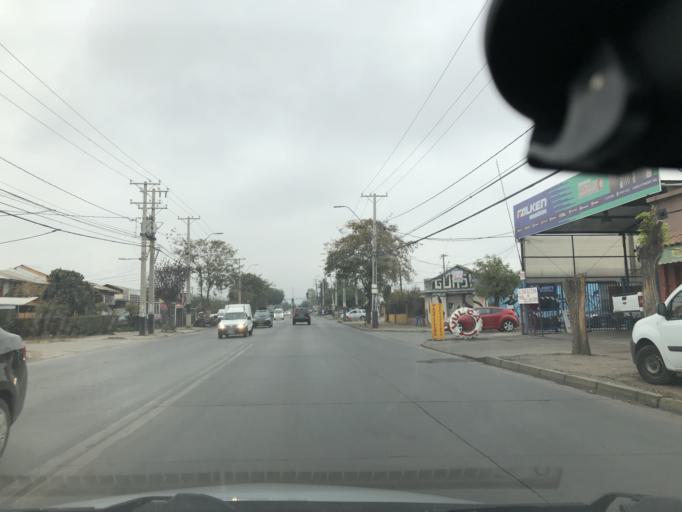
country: CL
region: Santiago Metropolitan
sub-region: Provincia de Santiago
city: La Pintana
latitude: -33.5823
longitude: -70.6043
